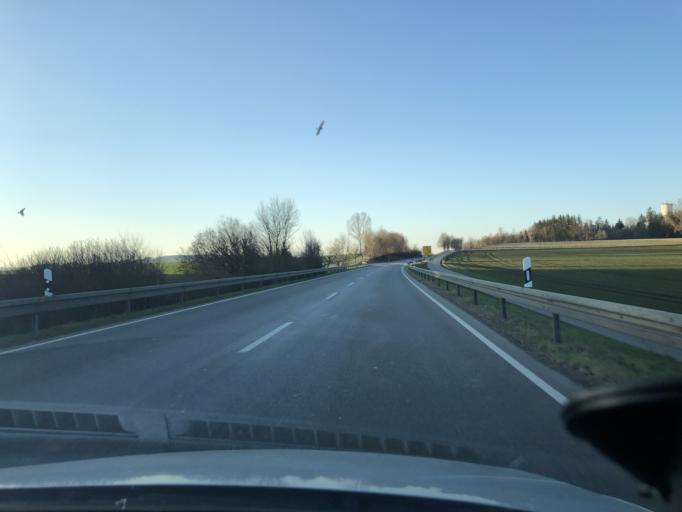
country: DE
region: Baden-Wuerttemberg
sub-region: Freiburg Region
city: Hufingen
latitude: 47.9114
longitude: 8.5054
